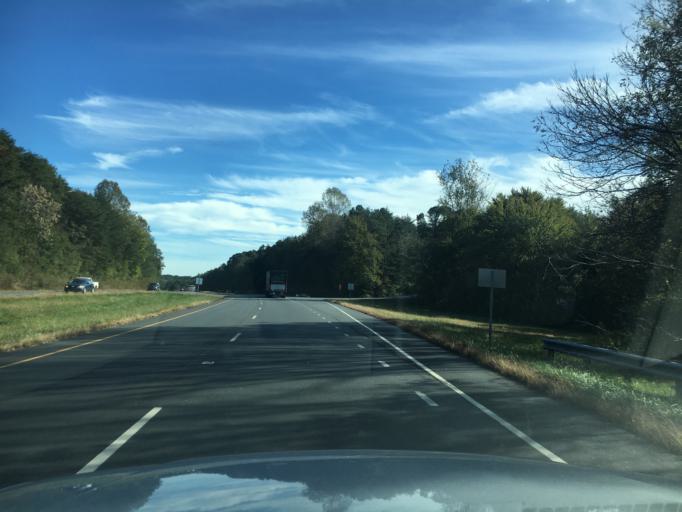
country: US
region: North Carolina
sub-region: Rutherford County
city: Spindale
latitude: 35.3537
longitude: -81.9433
